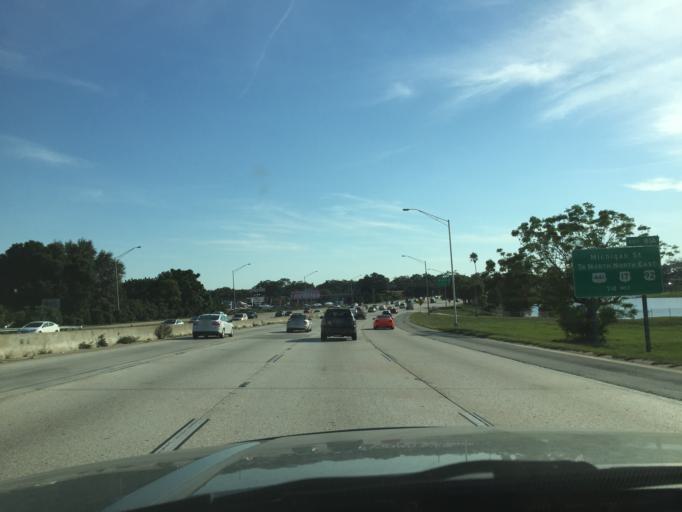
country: US
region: Florida
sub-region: Orange County
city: Orlando
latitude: 28.5189
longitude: -81.3865
